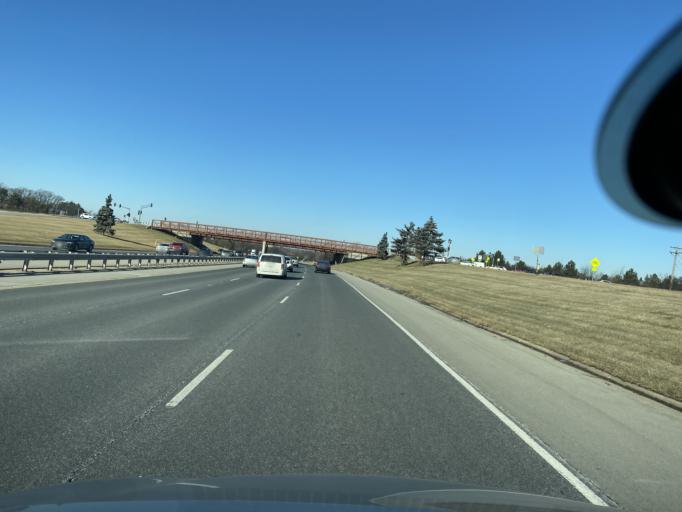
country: US
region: Illinois
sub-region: DuPage County
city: Oakbrook Terrace
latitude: 41.8308
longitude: -87.9543
